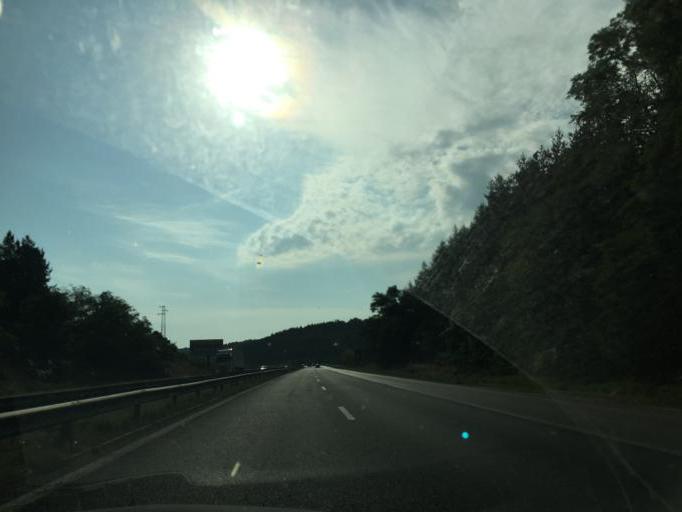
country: BG
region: Sofiya
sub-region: Obshtina Elin Pelin
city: Elin Pelin
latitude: 42.5854
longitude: 23.6364
